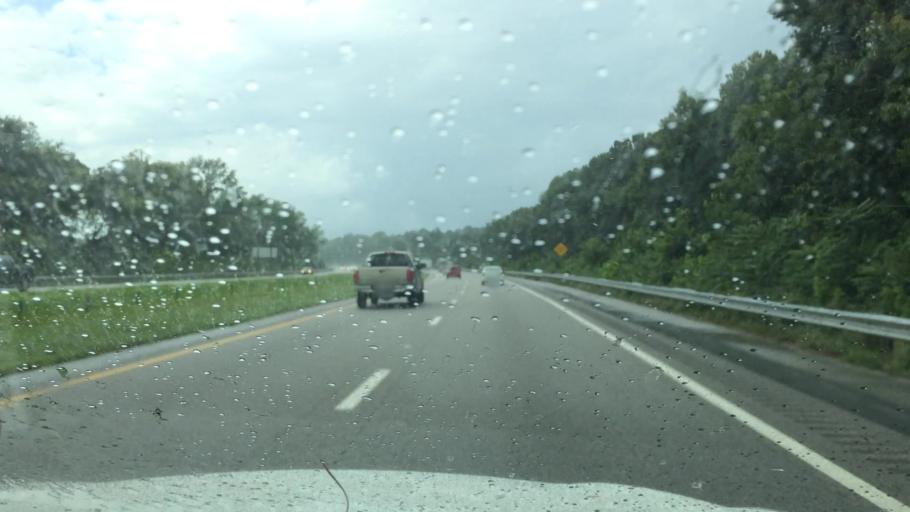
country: US
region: South Carolina
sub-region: Kershaw County
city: Camden
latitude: 34.2195
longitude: -80.6151
